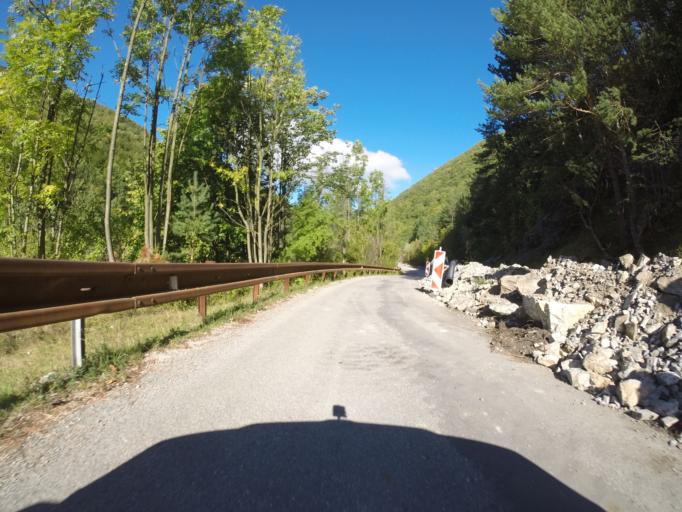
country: SK
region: Trenciansky
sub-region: Okres Povazska Bystrica
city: Povazska Bystrica
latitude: 48.9651
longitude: 18.4052
